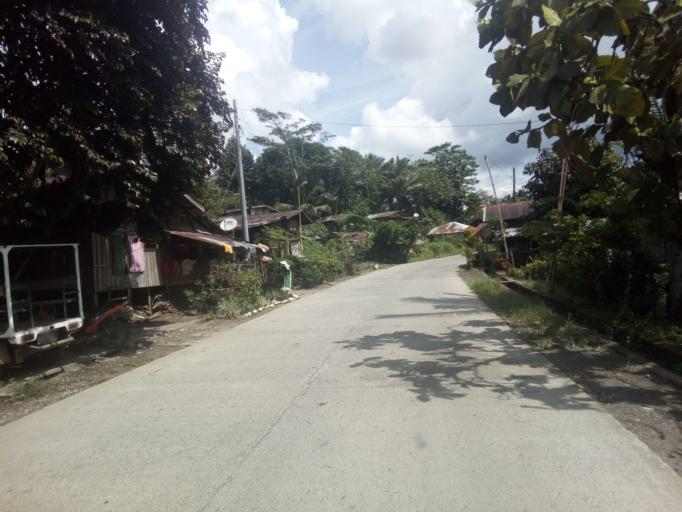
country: PH
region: Caraga
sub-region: Province of Agusan del Sur
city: Santa Josefa
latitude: 7.9895
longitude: 126.0343
